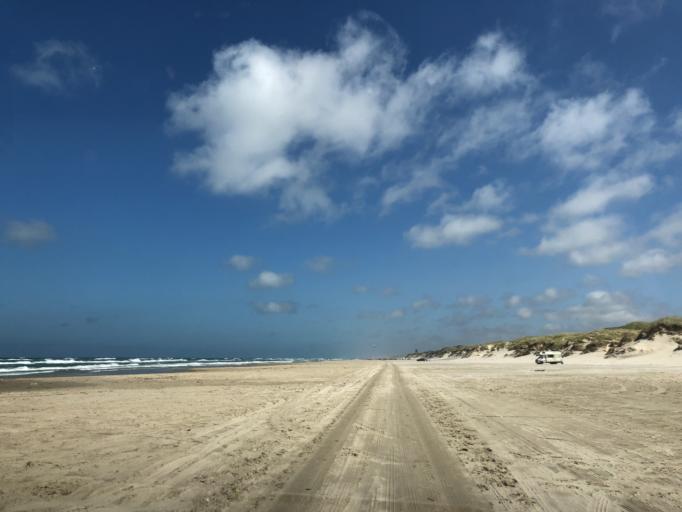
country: DK
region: North Denmark
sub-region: Jammerbugt Kommune
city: Pandrup
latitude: 57.2442
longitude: 9.5657
